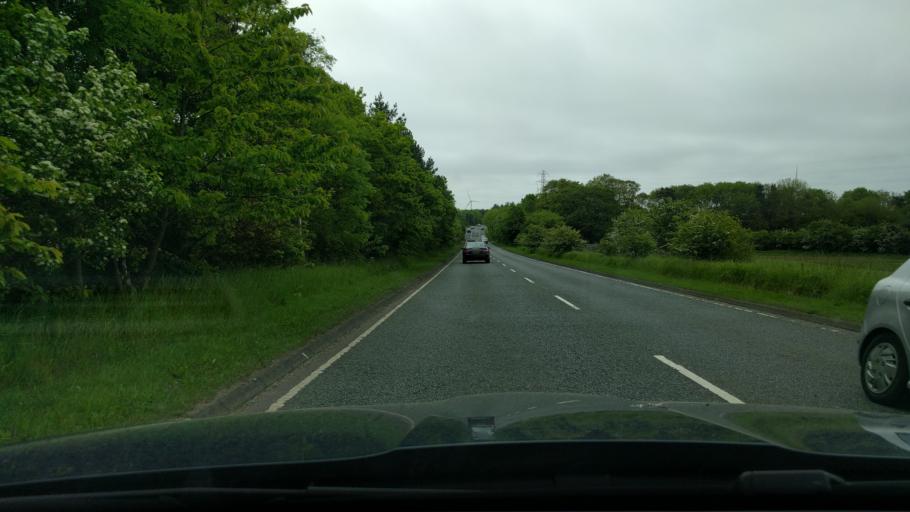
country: GB
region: England
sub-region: Northumberland
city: Cresswell
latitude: 55.2196
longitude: -1.5721
